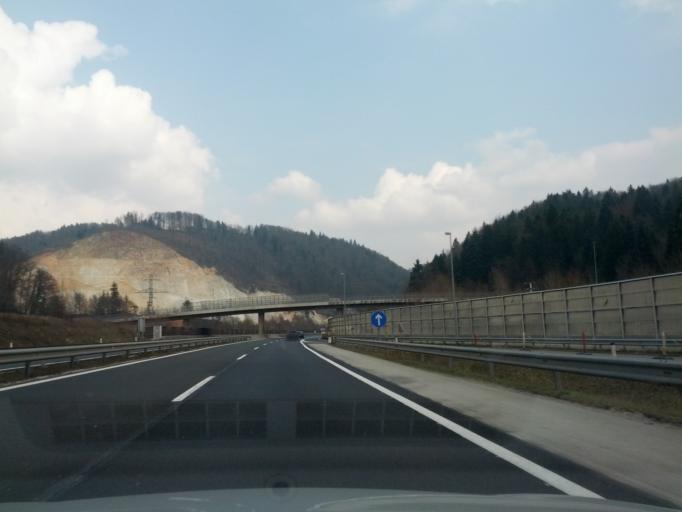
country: SI
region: Lukovica
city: Lukovica pri Domzalah
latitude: 46.1691
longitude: 14.6964
